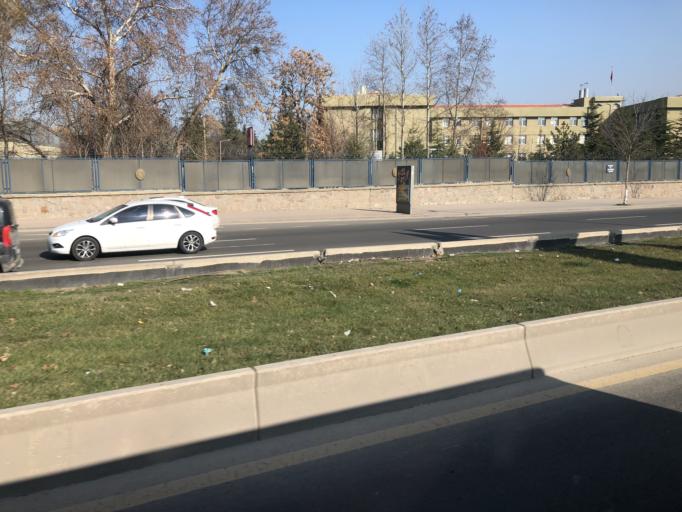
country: TR
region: Ankara
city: Ankara
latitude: 39.9625
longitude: 32.8444
